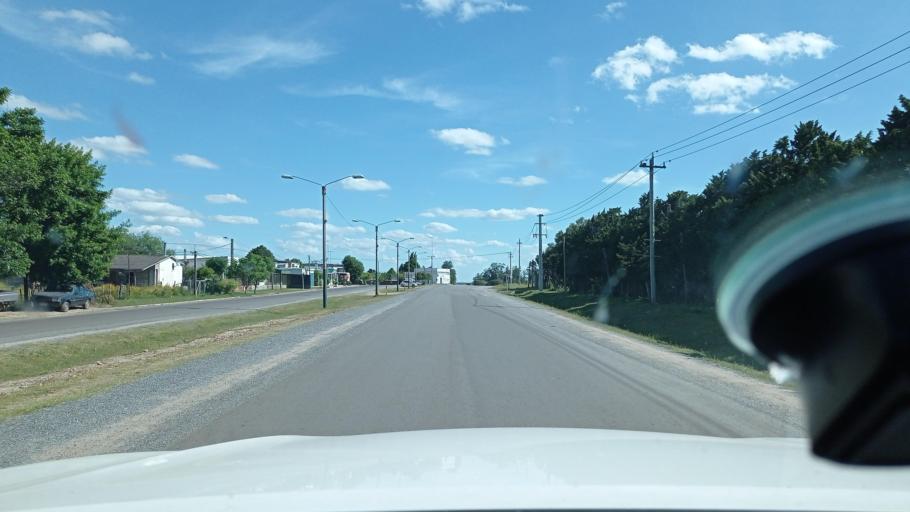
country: UY
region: Florida
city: Florida
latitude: -34.0894
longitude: -56.2383
